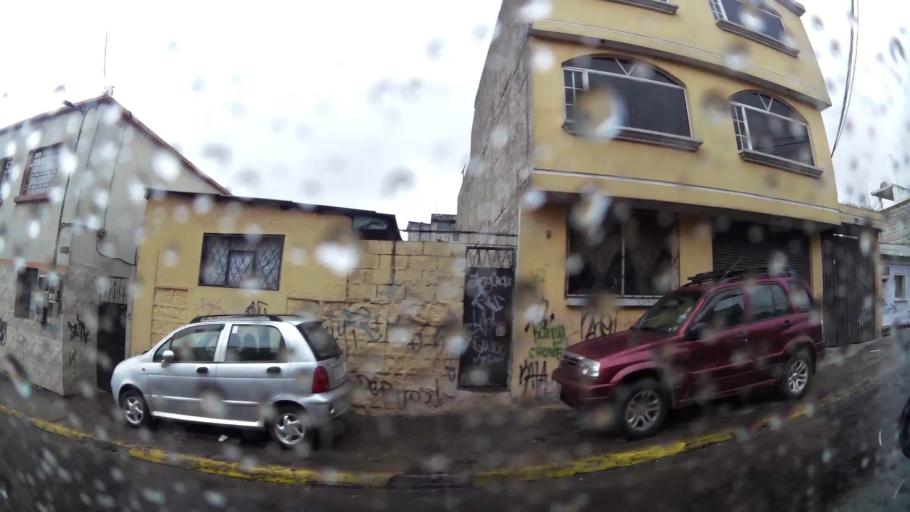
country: EC
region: Pichincha
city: Quito
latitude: -0.1082
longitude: -78.4966
